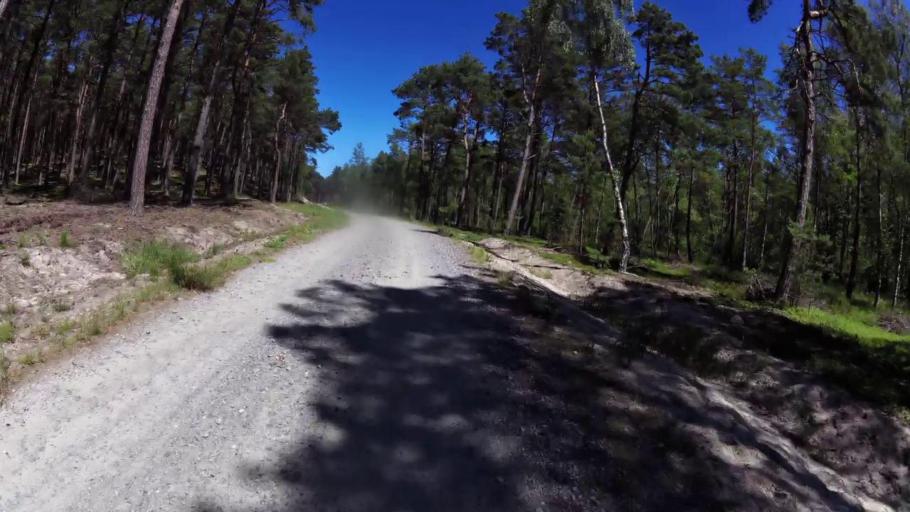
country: PL
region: West Pomeranian Voivodeship
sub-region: Powiat gryficki
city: Trzebiatow
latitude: 54.1075
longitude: 15.1951
